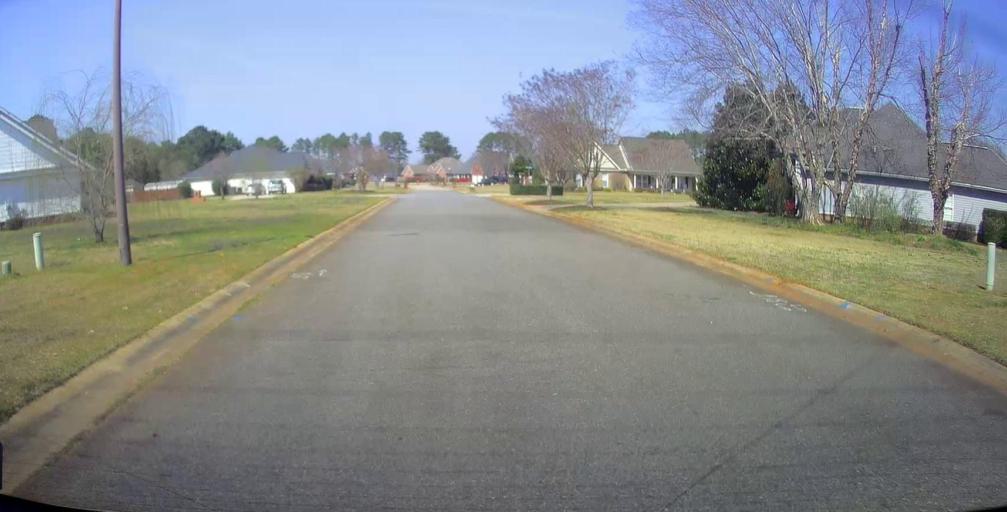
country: US
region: Georgia
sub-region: Houston County
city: Centerville
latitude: 32.5822
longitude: -83.7140
